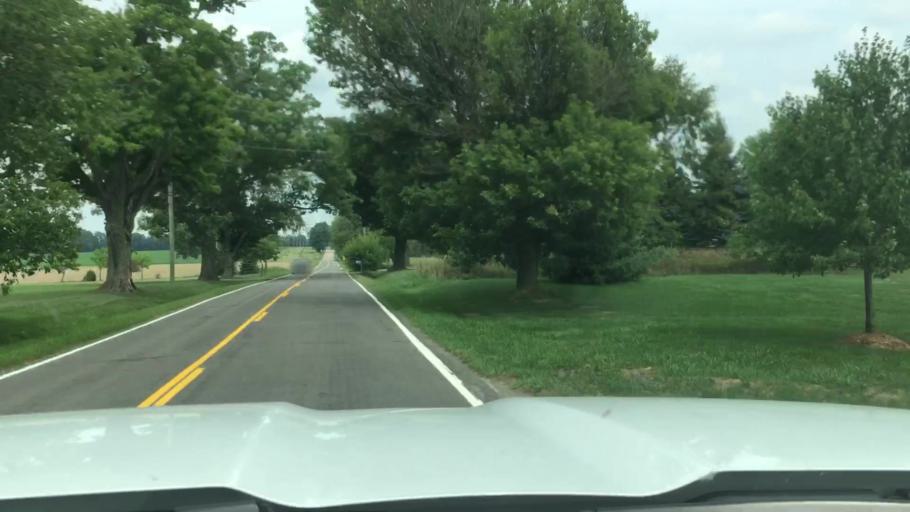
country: US
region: Michigan
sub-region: Ingham County
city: Webberville
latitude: 42.6888
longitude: -84.1901
